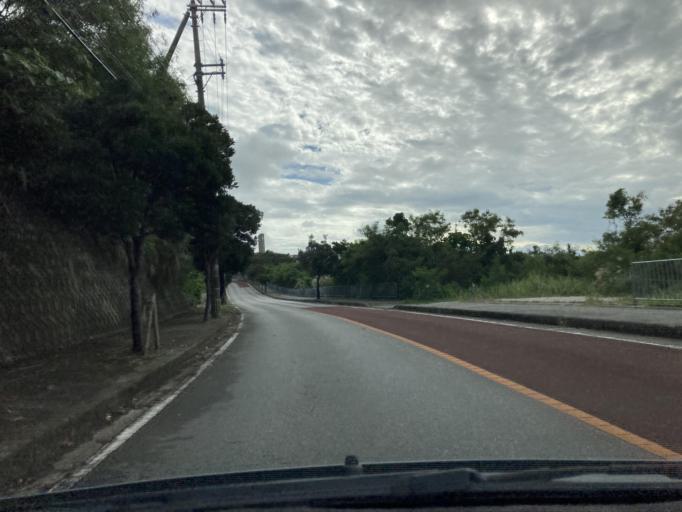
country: JP
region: Okinawa
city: Tomigusuku
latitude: 26.1826
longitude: 127.7463
